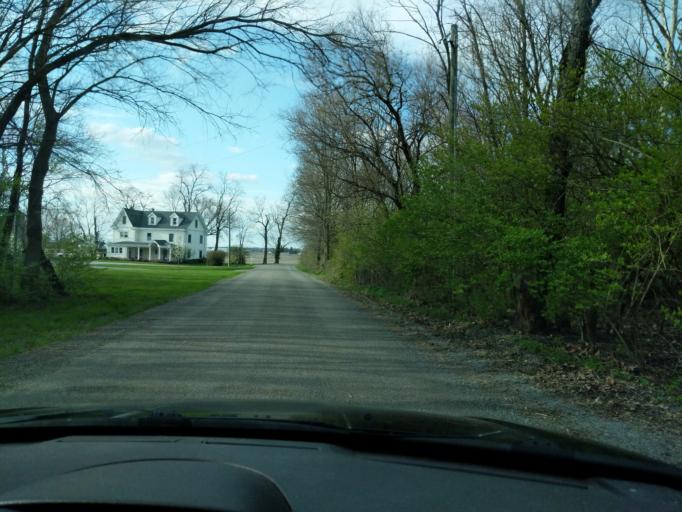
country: US
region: Ohio
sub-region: Champaign County
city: Urbana
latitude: 40.1403
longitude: -83.6874
